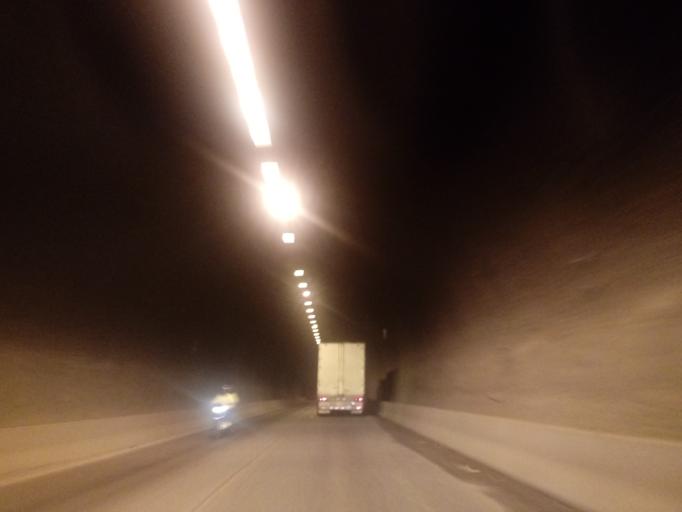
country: CR
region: Heredia
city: Angeles
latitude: 10.0614
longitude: -84.0079
